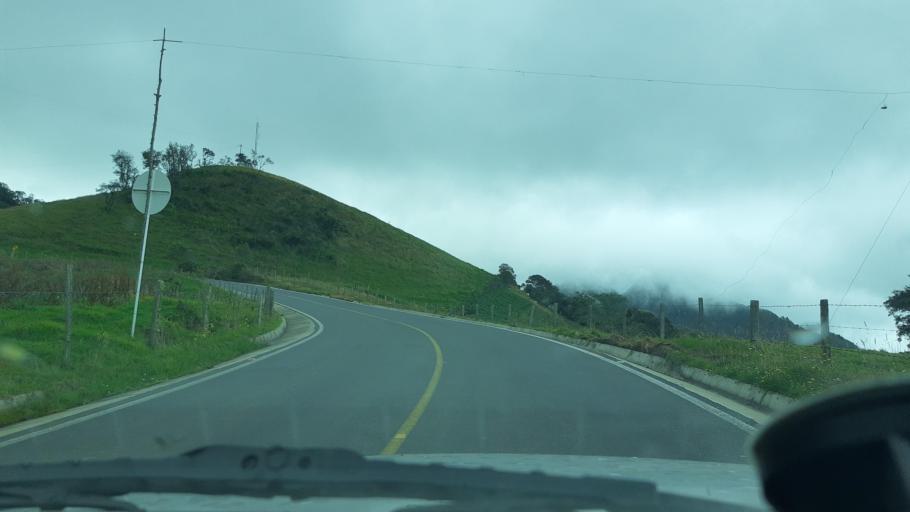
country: CO
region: Cundinamarca
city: Umbita
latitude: 5.2254
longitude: -73.4723
